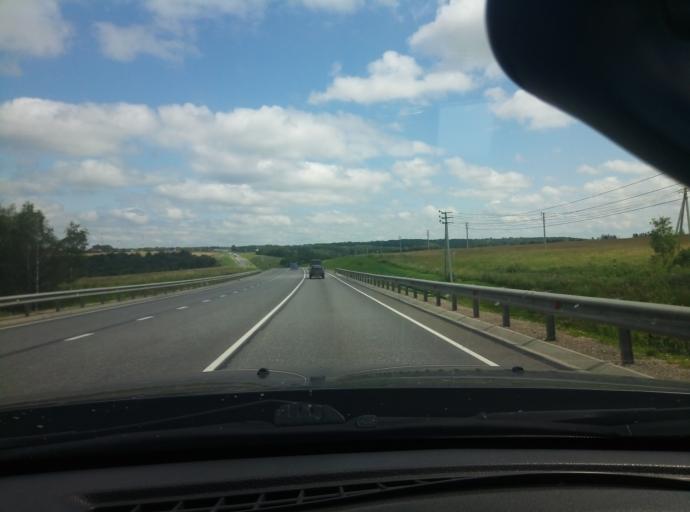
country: RU
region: Kaluga
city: Kaluga
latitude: 54.4329
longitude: 36.4315
